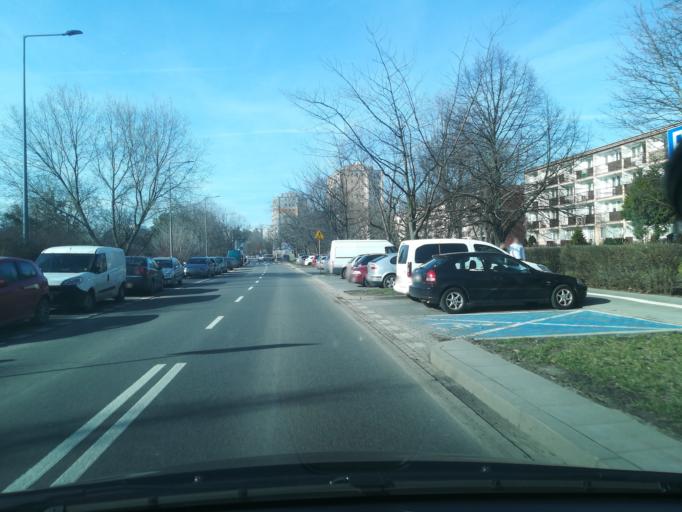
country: PL
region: Masovian Voivodeship
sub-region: Warszawa
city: Praga Poludnie
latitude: 52.2377
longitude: 21.0757
